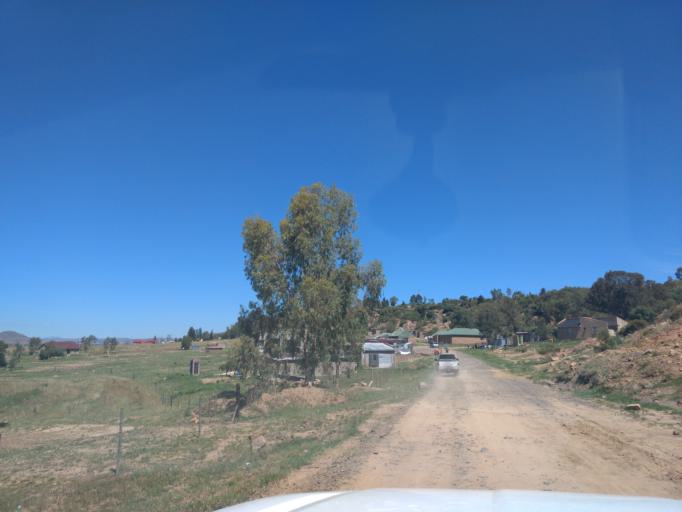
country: LS
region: Maseru
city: Maseru
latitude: -29.4916
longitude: 27.3709
